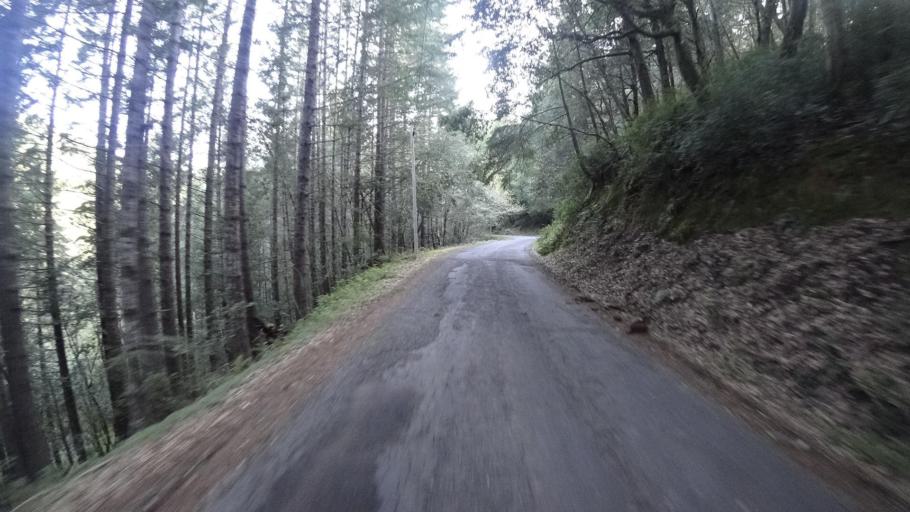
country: US
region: California
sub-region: Humboldt County
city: Bayside
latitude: 40.6987
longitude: -123.9408
